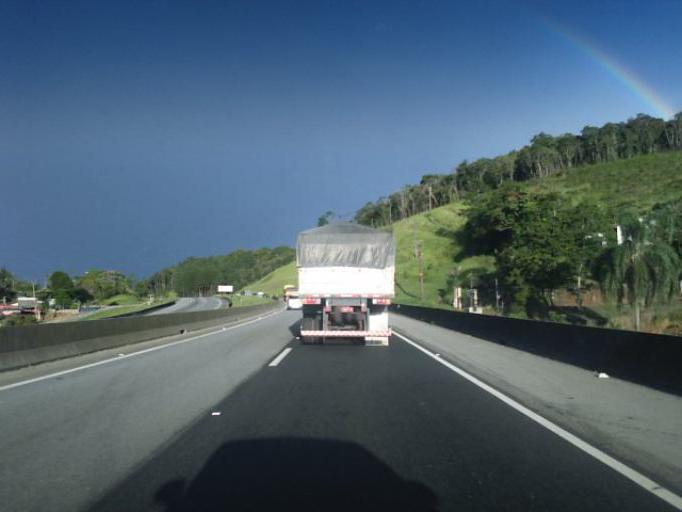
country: BR
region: Sao Paulo
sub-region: Juquitiba
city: Juquitiba
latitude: -23.9753
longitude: -47.1410
